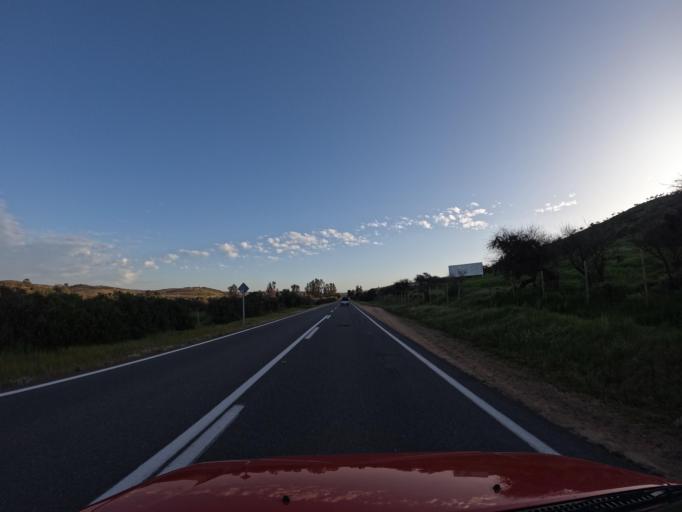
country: CL
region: O'Higgins
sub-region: Provincia de Colchagua
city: Santa Cruz
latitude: -34.2878
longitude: -71.7293
